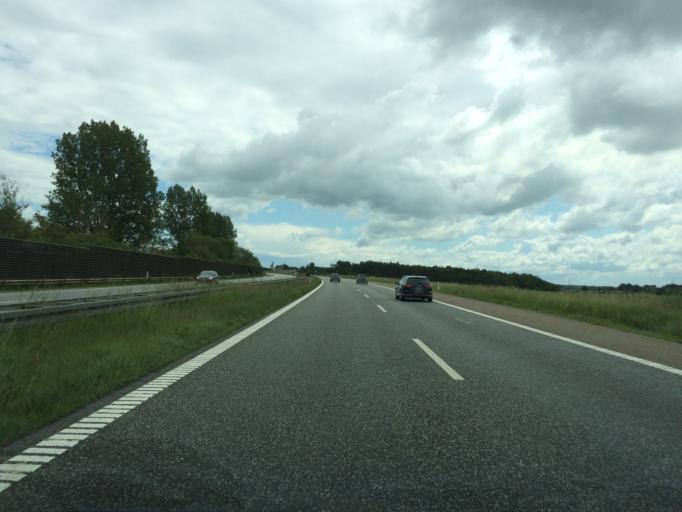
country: DK
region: Zealand
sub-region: Lejre Kommune
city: Ejby
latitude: 55.6458
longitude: 11.8164
